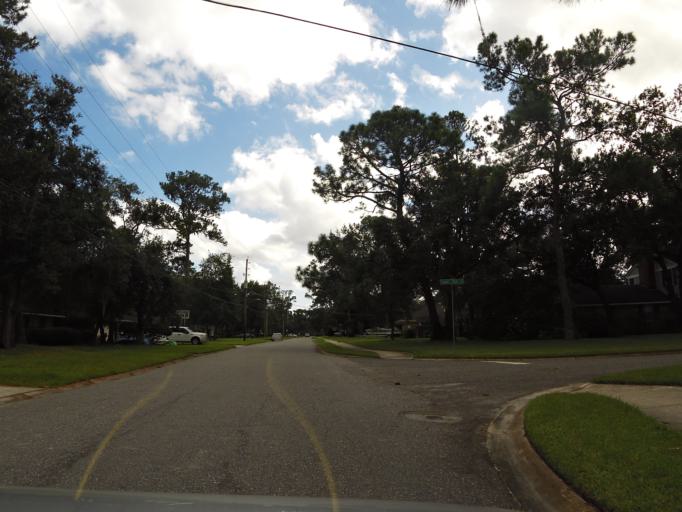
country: US
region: Florida
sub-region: Duval County
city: Jacksonville
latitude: 30.2566
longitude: -81.7012
